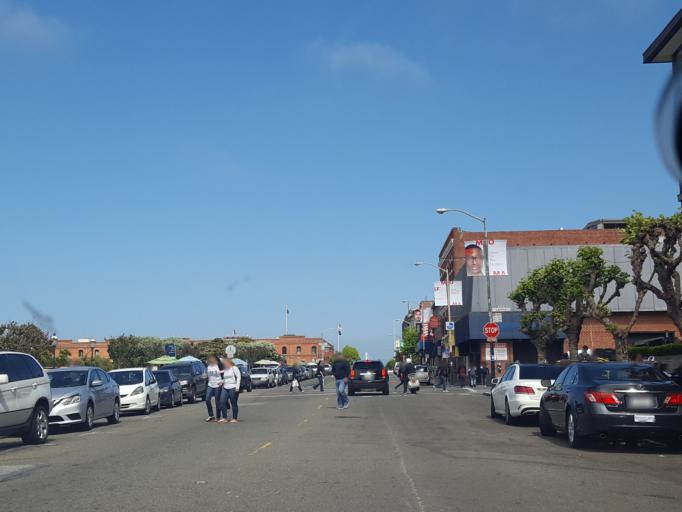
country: US
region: California
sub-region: San Francisco County
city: San Francisco
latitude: 37.8063
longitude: -122.4229
